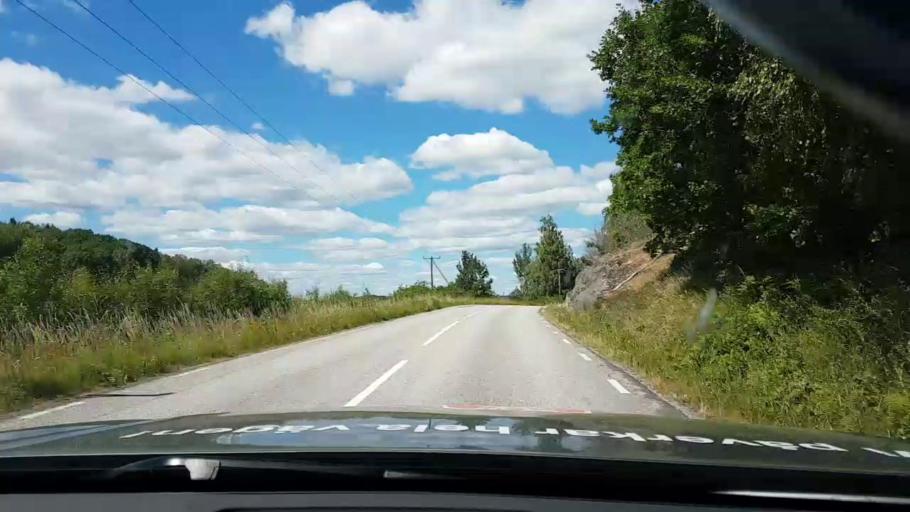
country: SE
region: Kalmar
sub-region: Vasterviks Kommun
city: Overum
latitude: 58.0494
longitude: 16.4081
